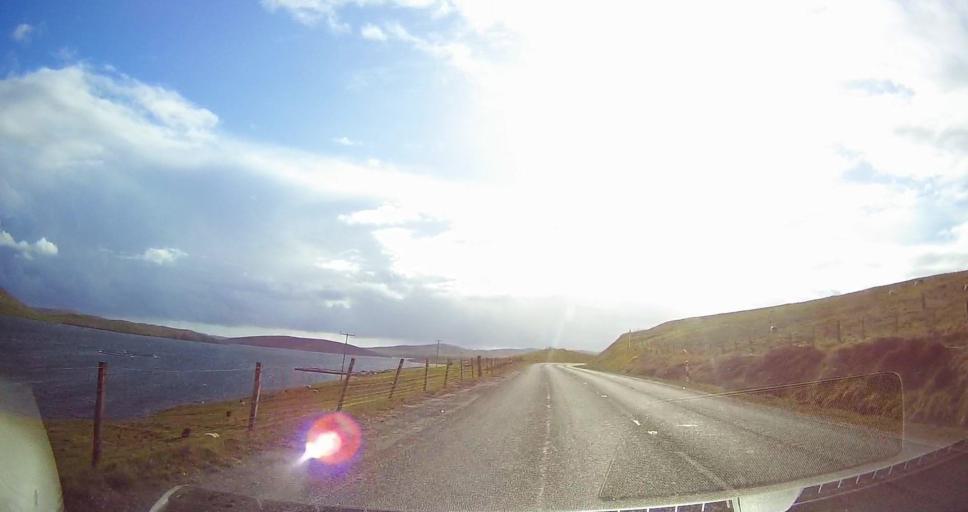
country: GB
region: Scotland
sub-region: Shetland Islands
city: Lerwick
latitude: 60.3705
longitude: -1.3066
